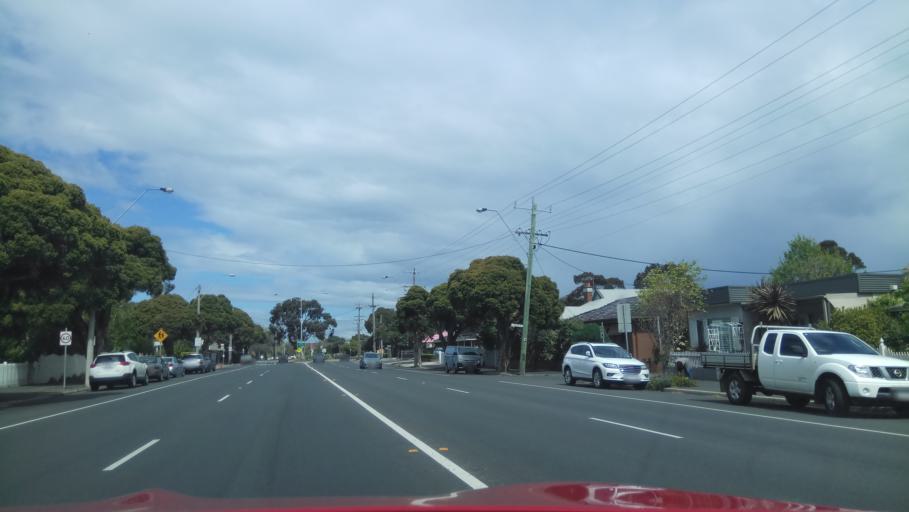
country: AU
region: Victoria
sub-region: Hobsons Bay
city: Williamstown
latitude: -37.8569
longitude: 144.8929
